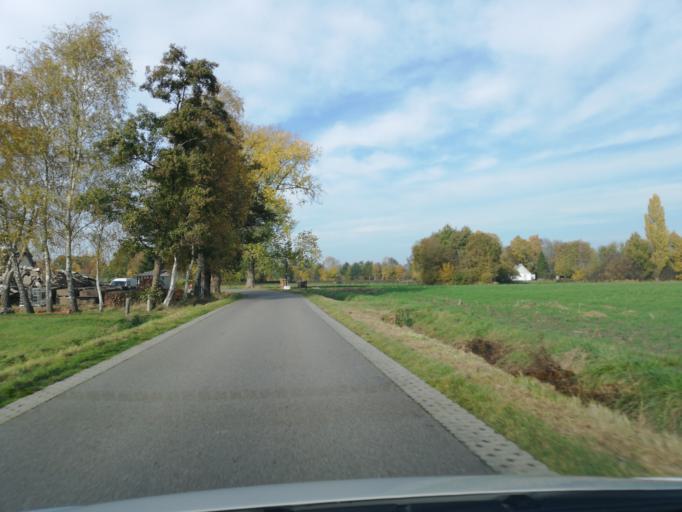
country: NL
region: Gelderland
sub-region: Gemeente Apeldoorn
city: Apeldoorn
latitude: 52.2433
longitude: 6.0257
